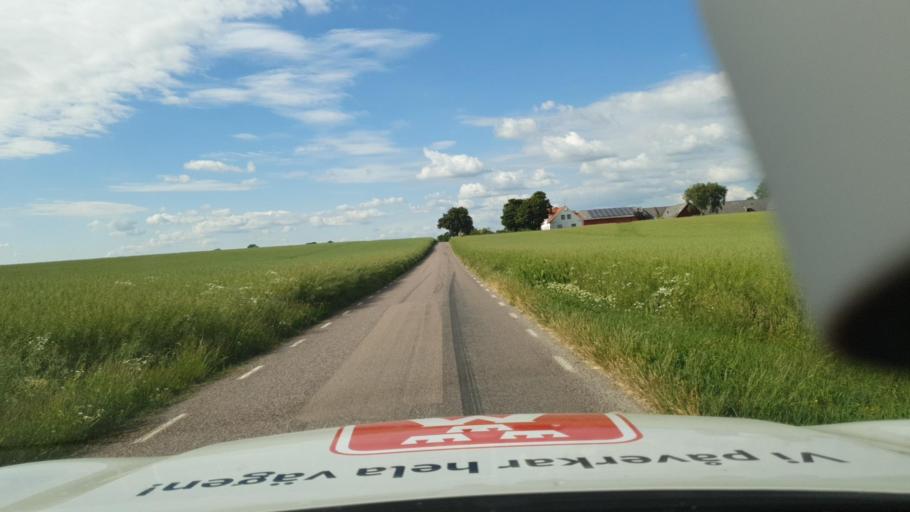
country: SE
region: Skane
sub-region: Skurups Kommun
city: Skurup
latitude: 55.4479
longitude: 13.5189
